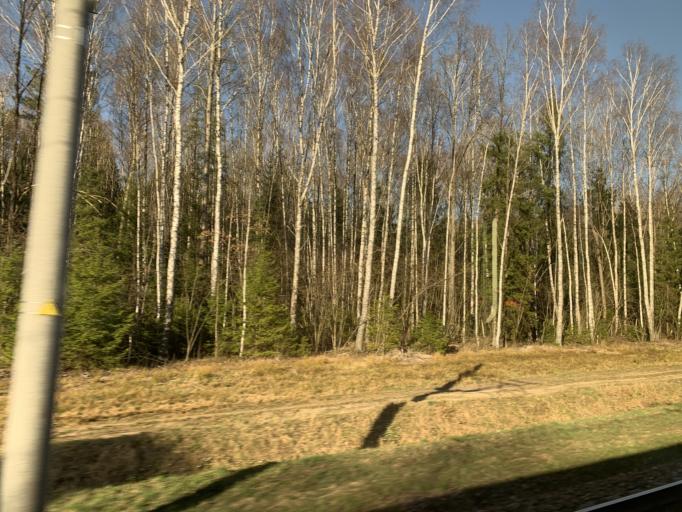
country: BY
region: Grodnenskaya
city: Smarhon'
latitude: 54.4862
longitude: 26.3162
